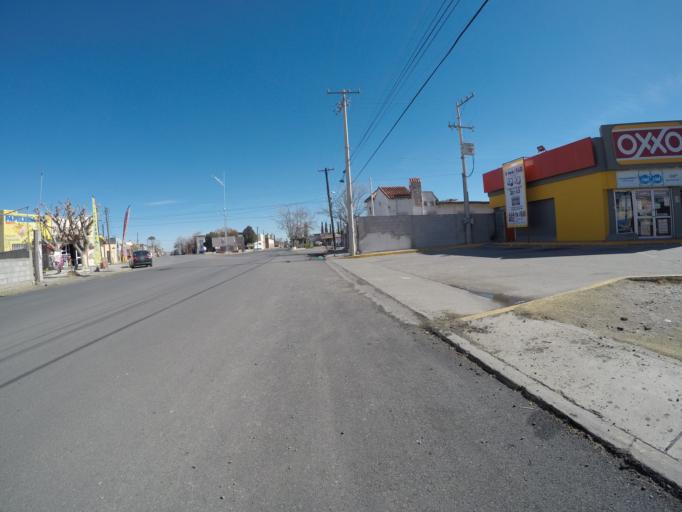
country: MX
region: Chihuahua
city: Ciudad Juarez
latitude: 31.7409
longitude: -106.4719
